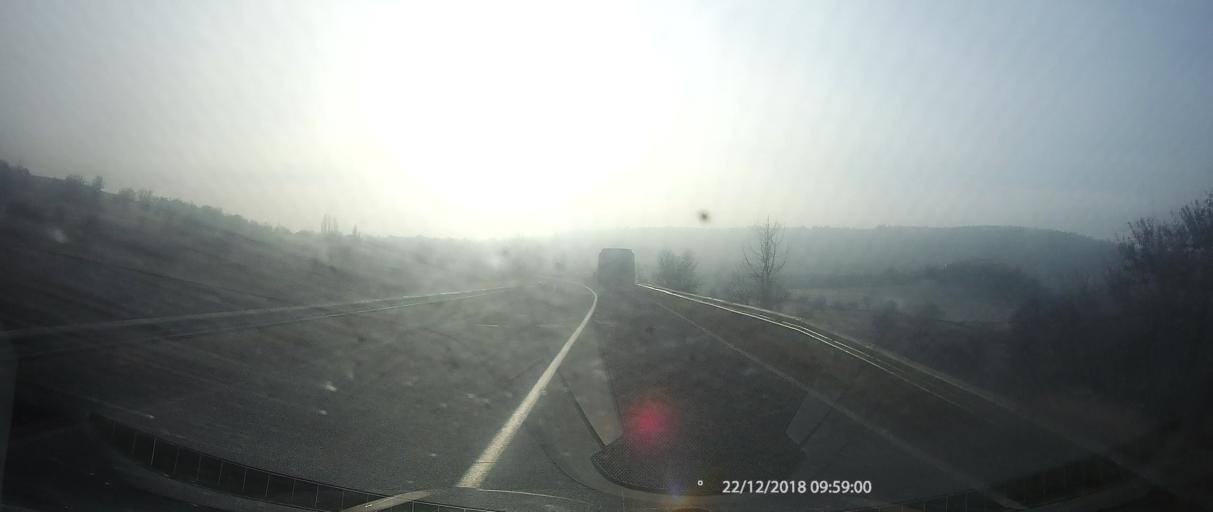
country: MK
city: Klechovce
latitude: 42.1540
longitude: 21.9516
